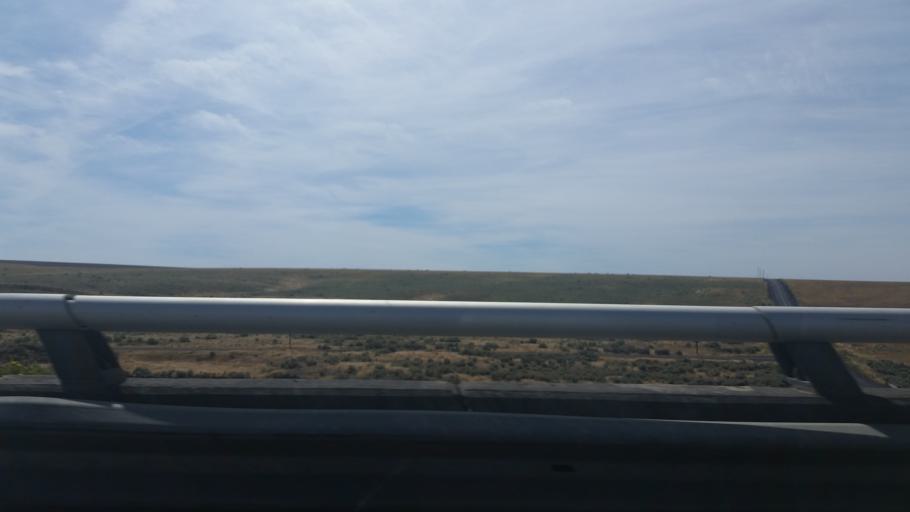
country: US
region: Washington
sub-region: Adams County
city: Ritzville
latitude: 47.1013
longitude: -118.6014
